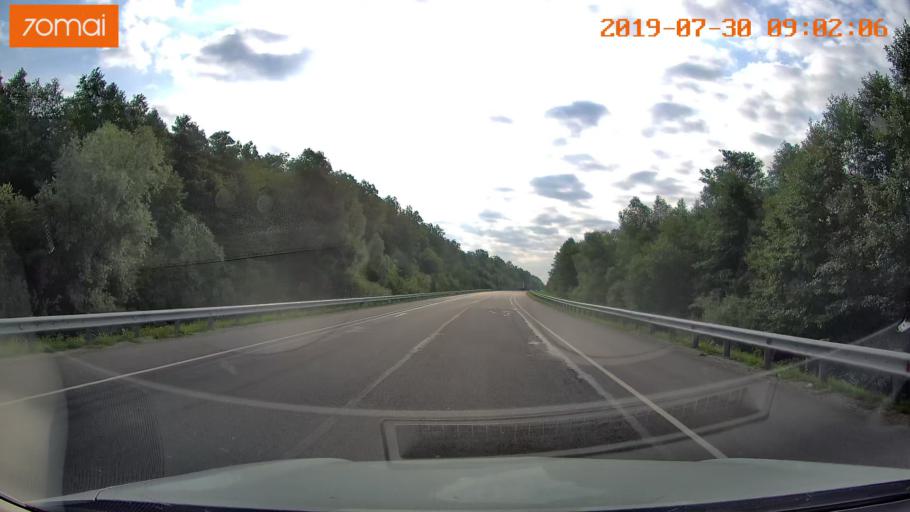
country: RU
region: Kaliningrad
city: Gusev
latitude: 54.6174
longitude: 22.2237
